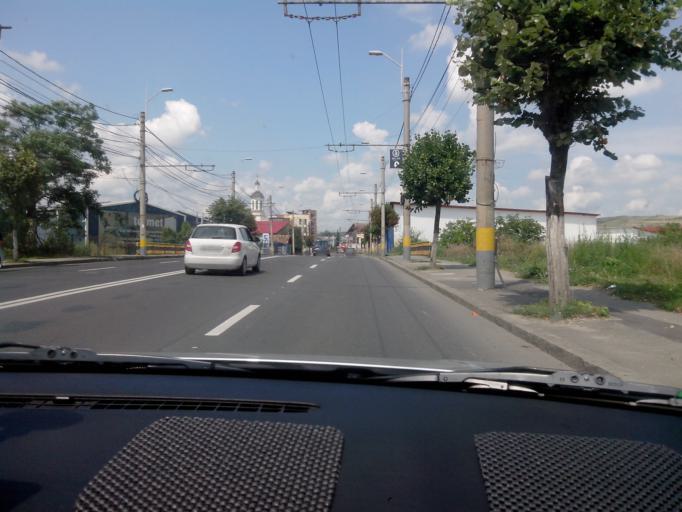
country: RO
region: Cluj
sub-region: Municipiul Cluj-Napoca
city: Cluj-Napoca
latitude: 46.7835
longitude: 23.6612
